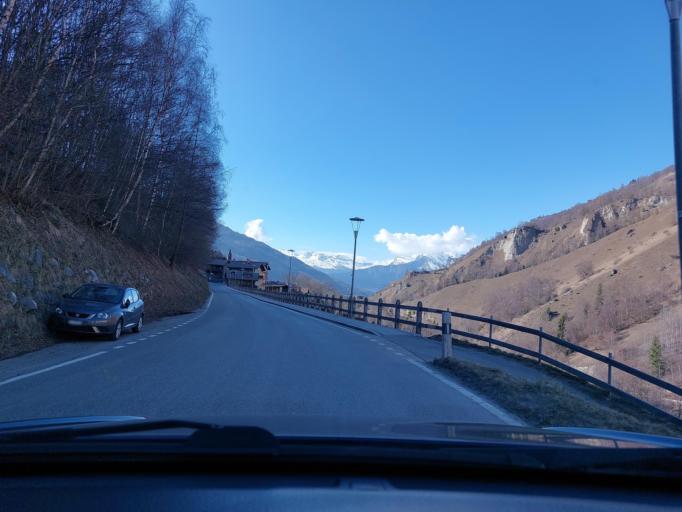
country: CH
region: Valais
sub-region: Herens District
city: Heremence
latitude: 46.1591
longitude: 7.4422
